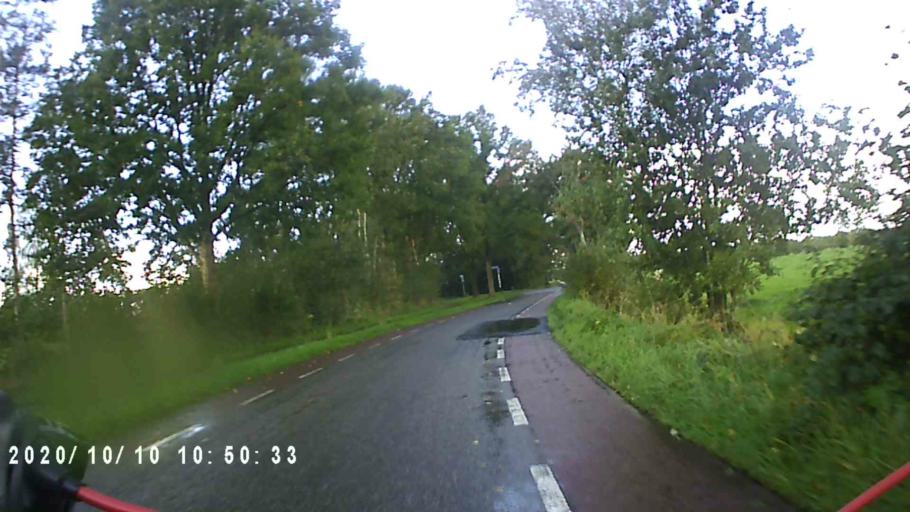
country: NL
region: Groningen
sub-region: Gemeente Grootegast
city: Grootegast
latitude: 53.1594
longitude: 6.2337
